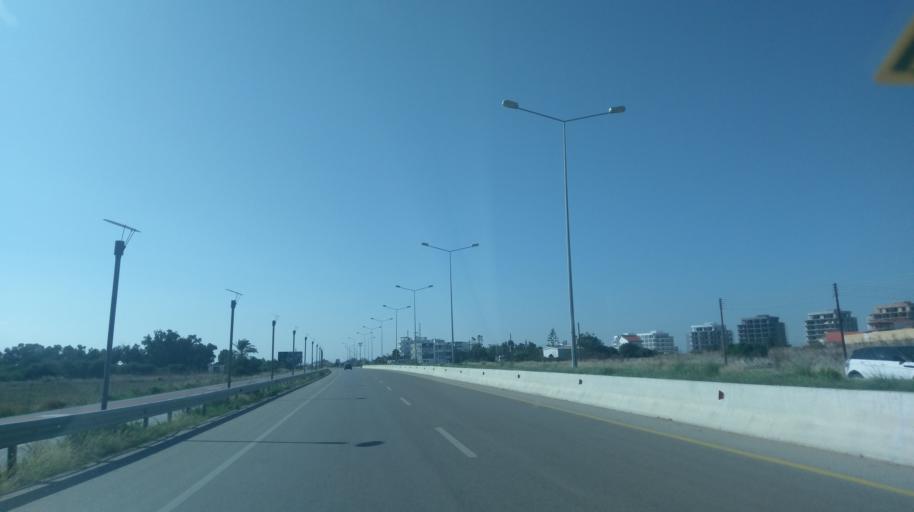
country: CY
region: Ammochostos
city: Trikomo
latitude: 35.2630
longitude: 33.9115
